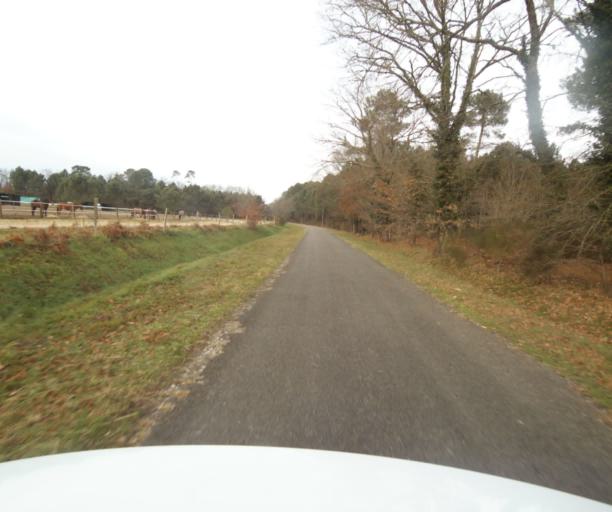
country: FR
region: Aquitaine
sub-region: Departement des Landes
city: Gabarret
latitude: 44.0945
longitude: 0.0606
